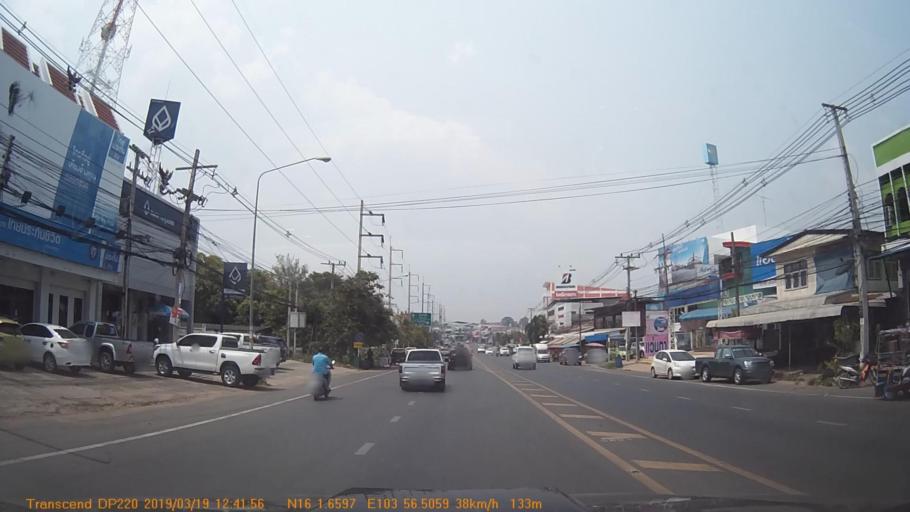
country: TH
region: Roi Et
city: Selaphum
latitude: 16.0278
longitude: 103.9417
